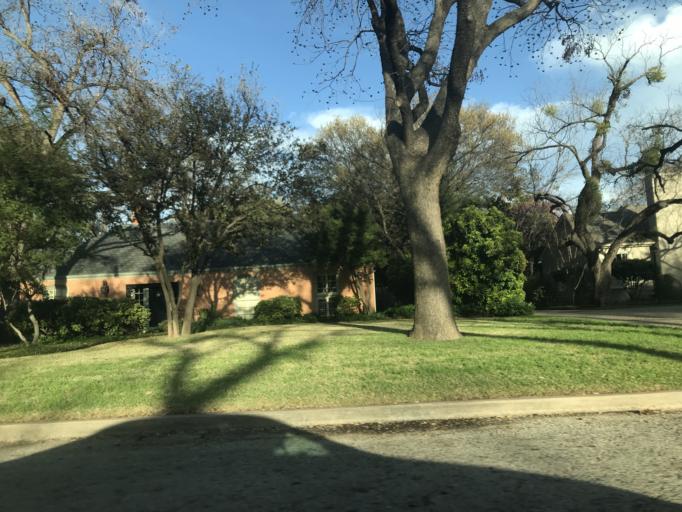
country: US
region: Texas
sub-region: Taylor County
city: Abilene
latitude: 32.4354
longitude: -99.7716
